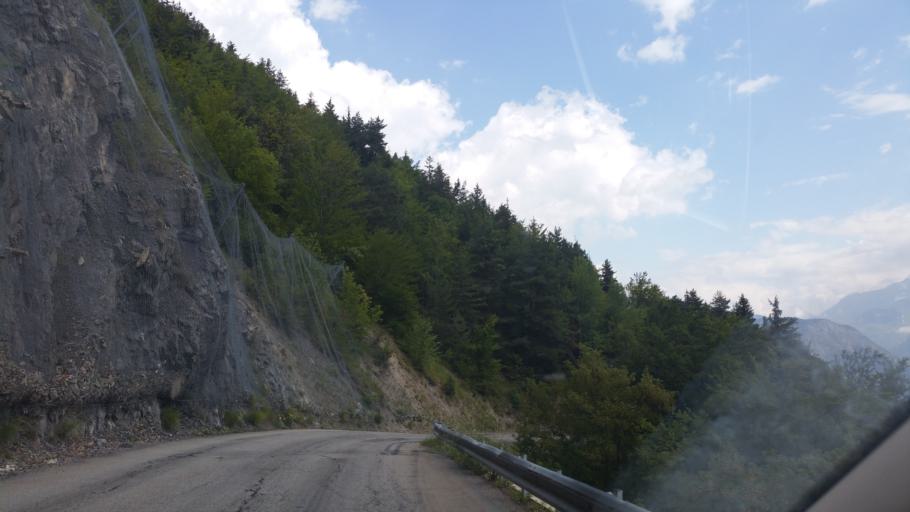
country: FR
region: Rhone-Alpes
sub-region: Departement de la Savoie
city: Saint-Jean-de-Maurienne
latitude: 45.2245
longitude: 6.3038
